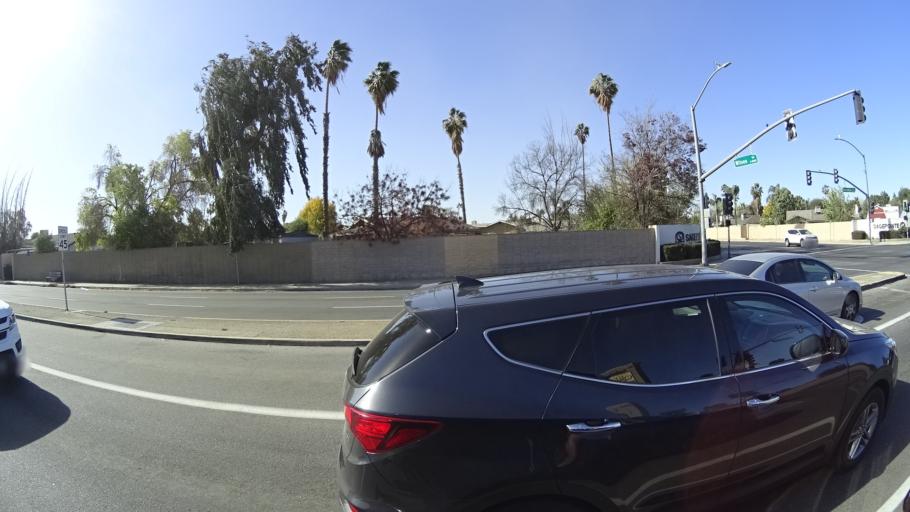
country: US
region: California
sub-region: Kern County
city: Bakersfield
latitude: 35.3320
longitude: -119.0580
